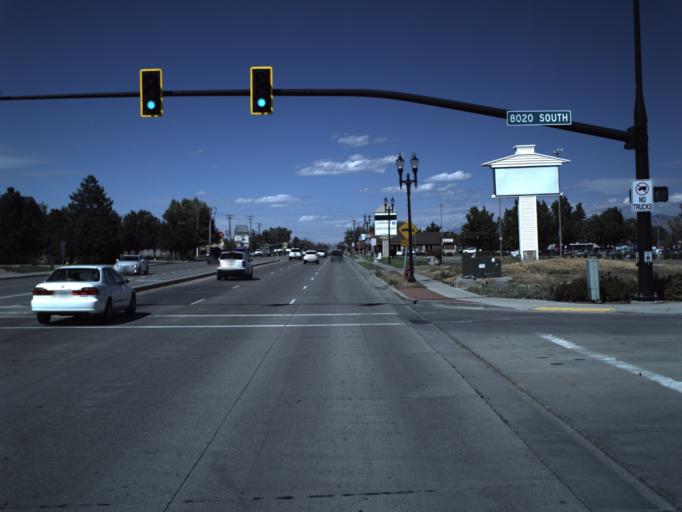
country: US
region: Utah
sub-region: Salt Lake County
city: West Jordan
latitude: 40.6055
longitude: -111.9386
